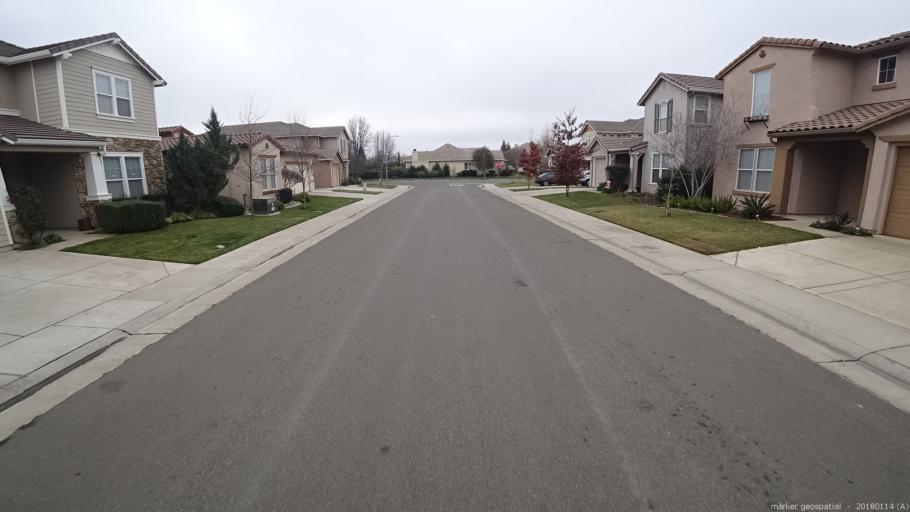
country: US
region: California
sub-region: Sacramento County
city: Gold River
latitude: 38.5462
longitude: -121.2268
